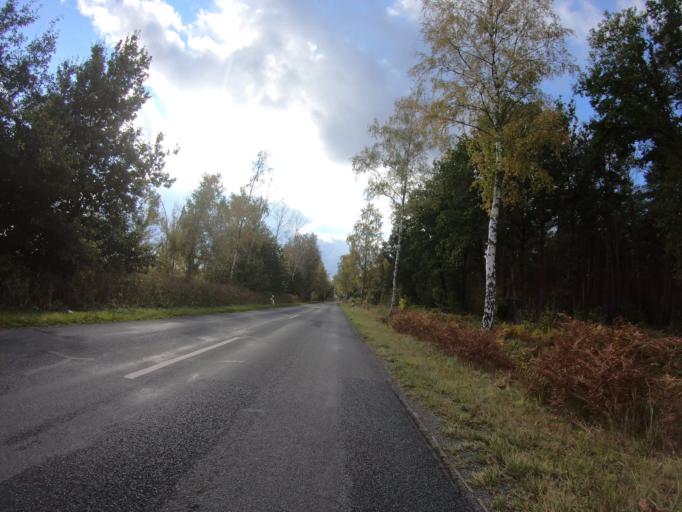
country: DE
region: Lower Saxony
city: Schoneworde
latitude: 52.5854
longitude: 10.6433
